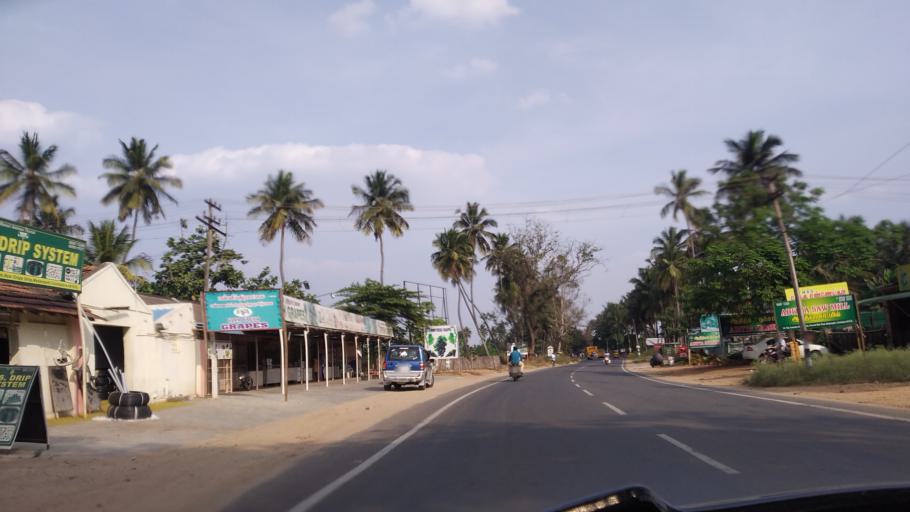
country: IN
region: Tamil Nadu
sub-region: Coimbatore
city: Perur
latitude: 10.9739
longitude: 76.8701
